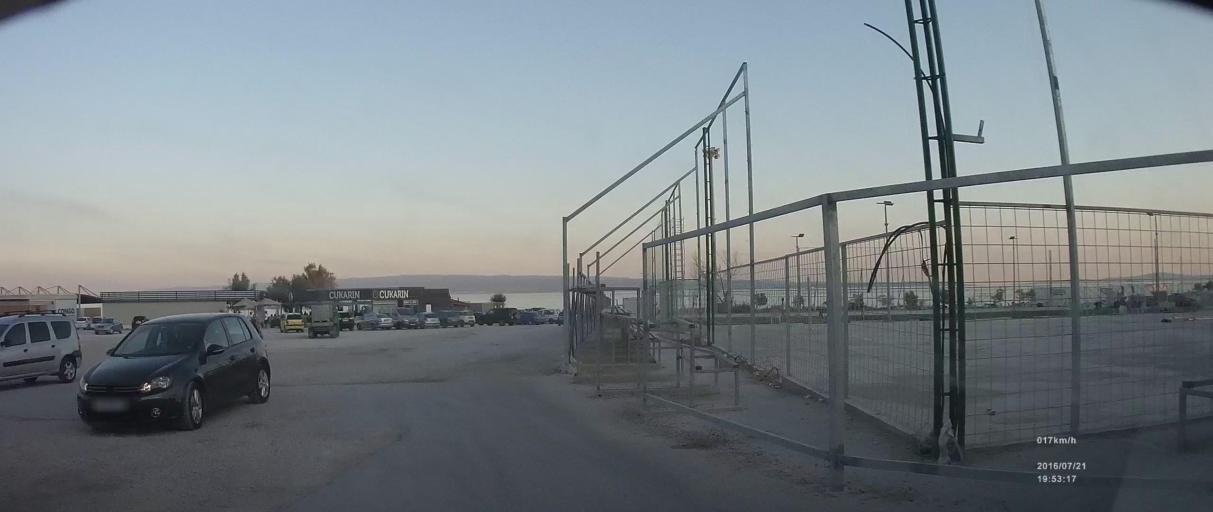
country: HR
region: Splitsko-Dalmatinska
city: Vranjic
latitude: 43.5031
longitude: 16.4766
